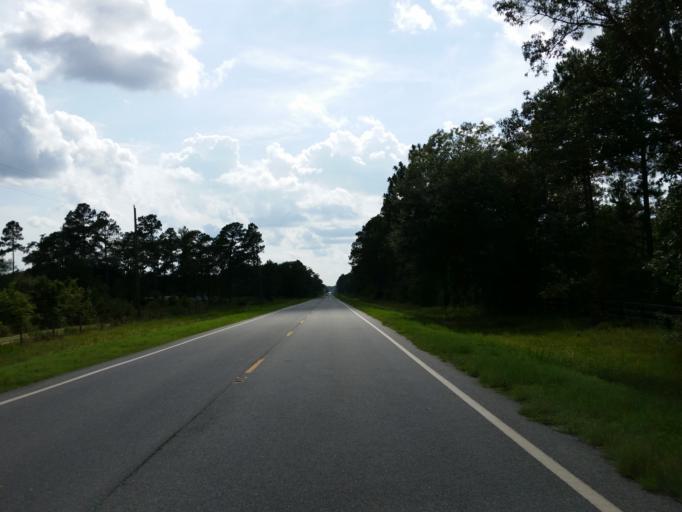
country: US
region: Georgia
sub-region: Lee County
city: Leesburg
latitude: 31.7279
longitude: -83.9715
